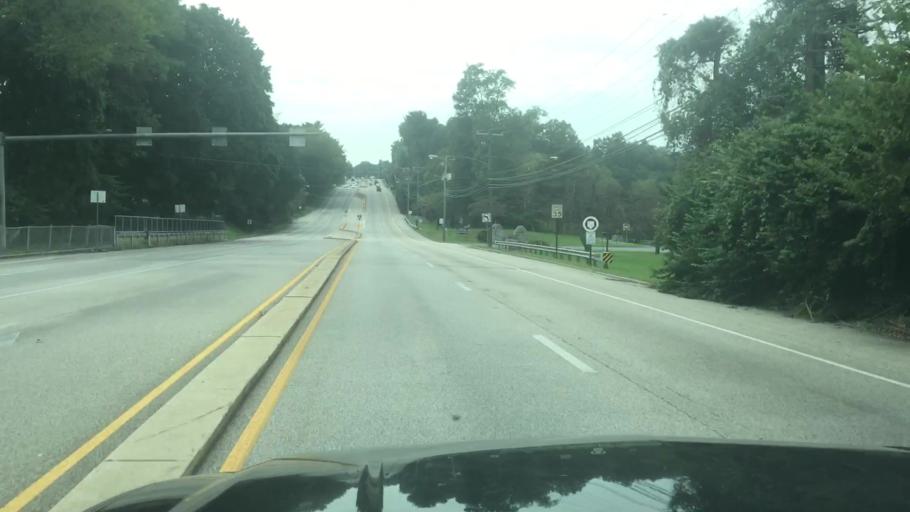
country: US
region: Pennsylvania
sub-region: Cumberland County
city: Camp Hill
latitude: 40.2489
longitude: -76.9248
